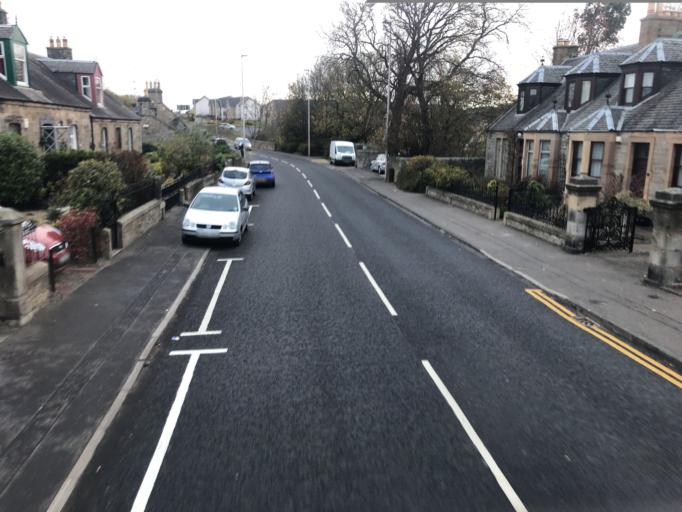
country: GB
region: Scotland
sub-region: Midlothian
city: Loanhead
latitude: 55.8837
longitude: -3.1573
